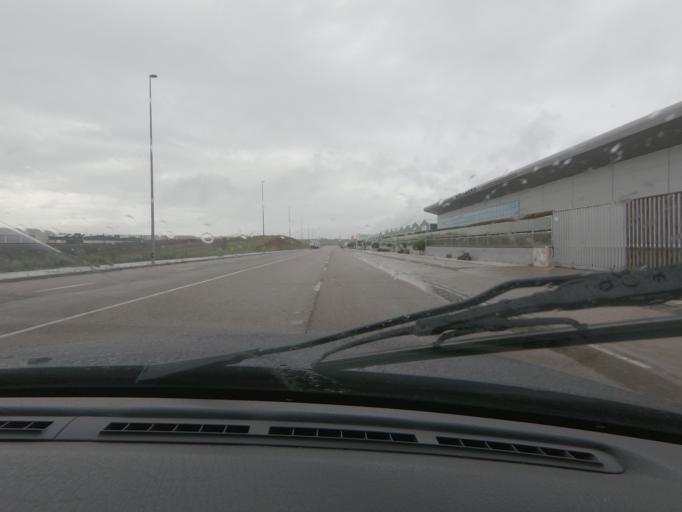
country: ES
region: Extremadura
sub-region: Provincia de Badajoz
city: Badajoz
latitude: 38.8984
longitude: -6.9935
